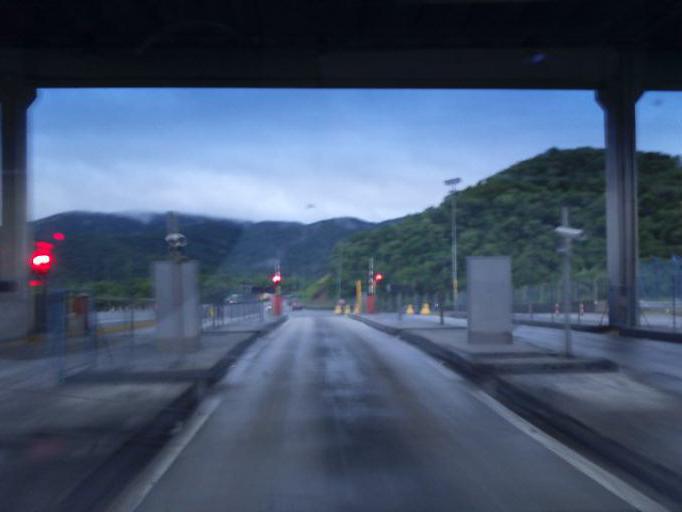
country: BR
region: Sao Paulo
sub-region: Miracatu
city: Miracatu
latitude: -24.1580
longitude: -47.3259
